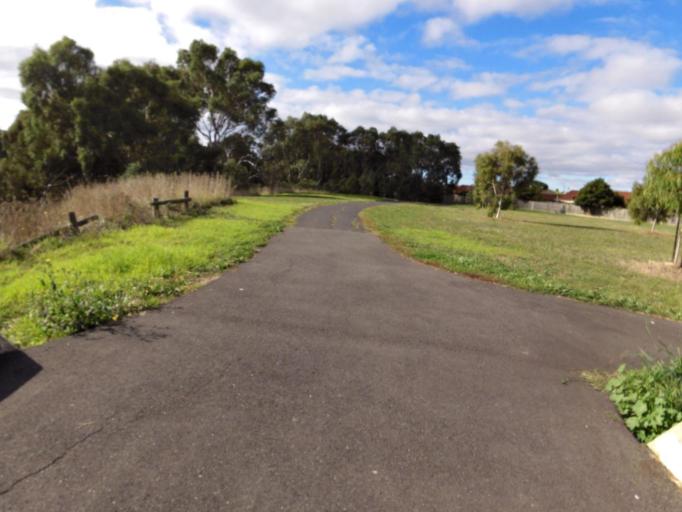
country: AU
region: Victoria
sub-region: Greater Geelong
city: Wandana Heights
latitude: -38.1955
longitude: 144.3266
